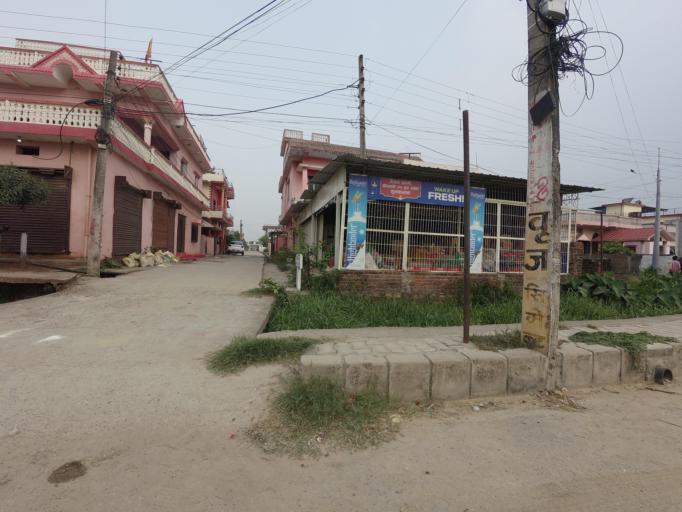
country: NP
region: Western Region
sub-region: Lumbini Zone
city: Bhairahawa
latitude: 27.5191
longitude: 83.4420
